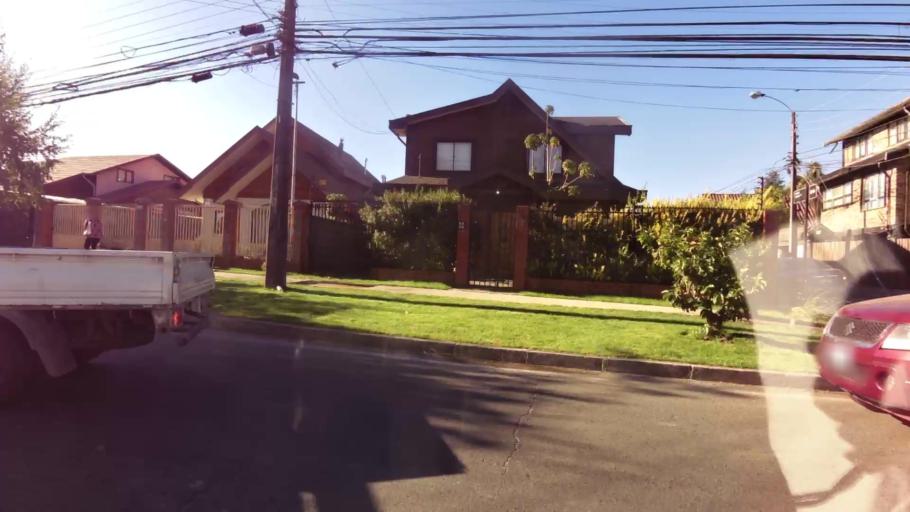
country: CL
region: Biobio
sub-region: Provincia de Concepcion
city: Concepcion
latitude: -36.8365
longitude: -73.1126
